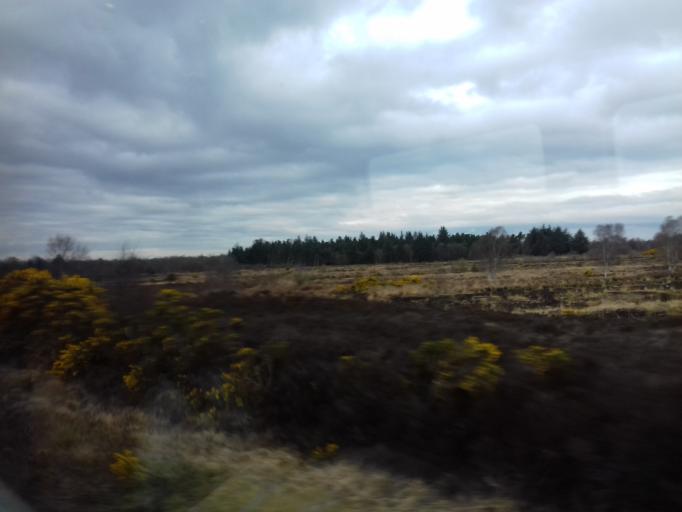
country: IE
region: Leinster
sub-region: An Longfort
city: Granard
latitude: 53.6636
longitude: -7.4650
